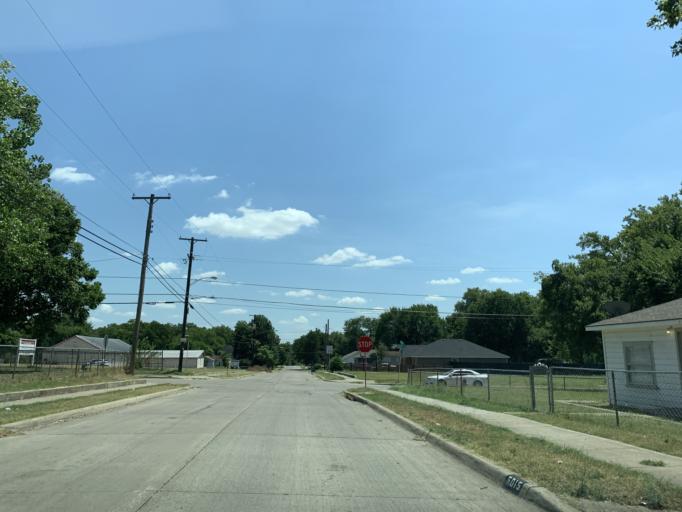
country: US
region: Texas
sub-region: Dallas County
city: Hutchins
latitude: 32.6889
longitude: -96.7791
